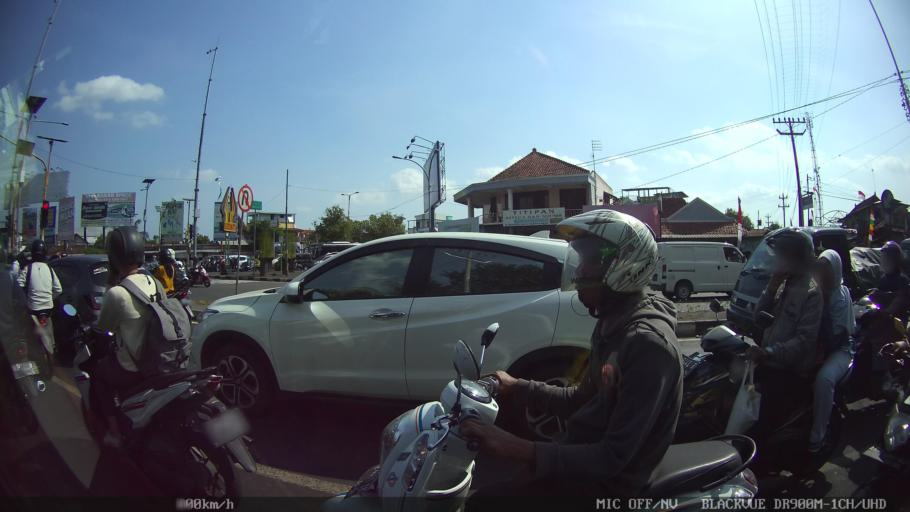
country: ID
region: Daerah Istimewa Yogyakarta
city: Sewon
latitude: -7.8361
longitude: 110.3917
